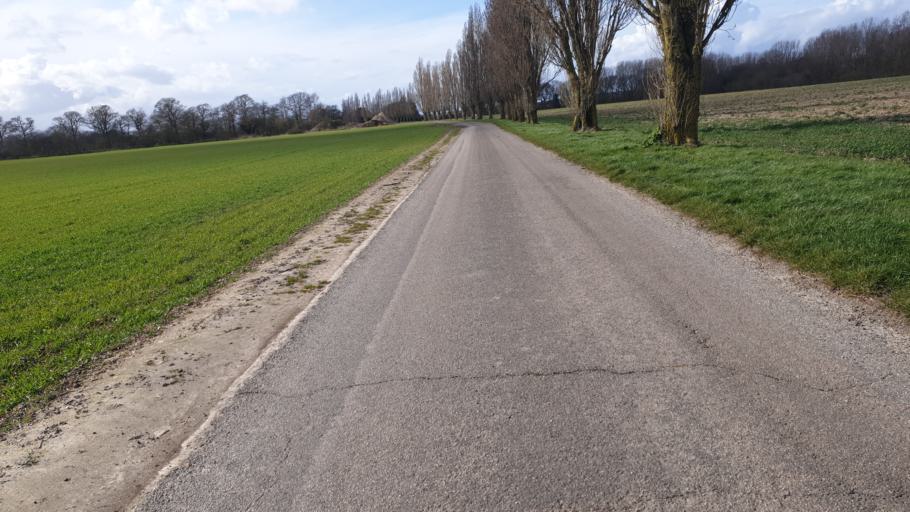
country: GB
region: England
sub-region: Essex
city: Little Clacton
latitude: 51.8504
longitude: 1.1348
